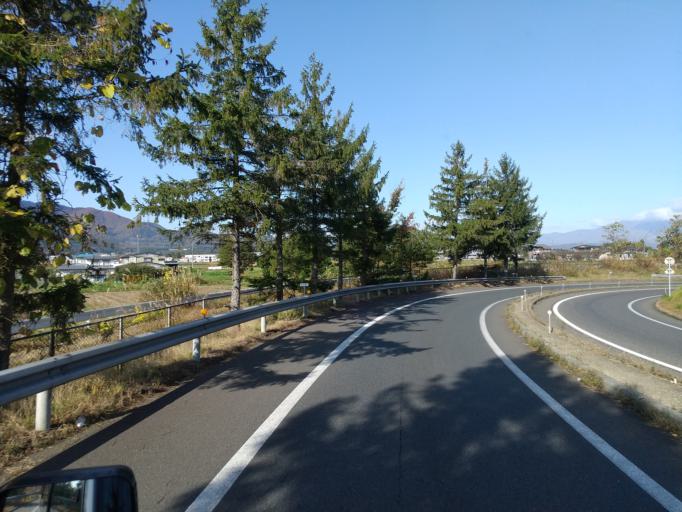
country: JP
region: Iwate
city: Morioka-shi
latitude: 39.6511
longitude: 141.1218
